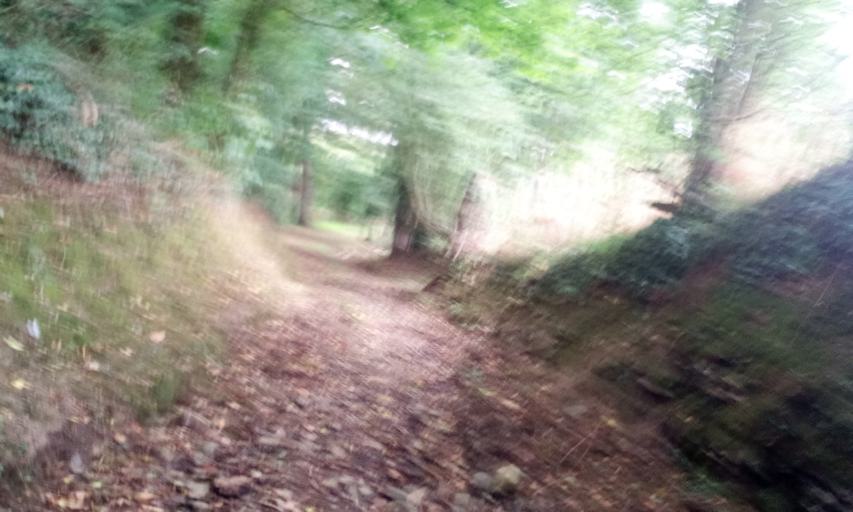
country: FR
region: Lower Normandy
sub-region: Departement du Calvados
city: Thury-Harcourt
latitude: 48.9856
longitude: -0.4272
